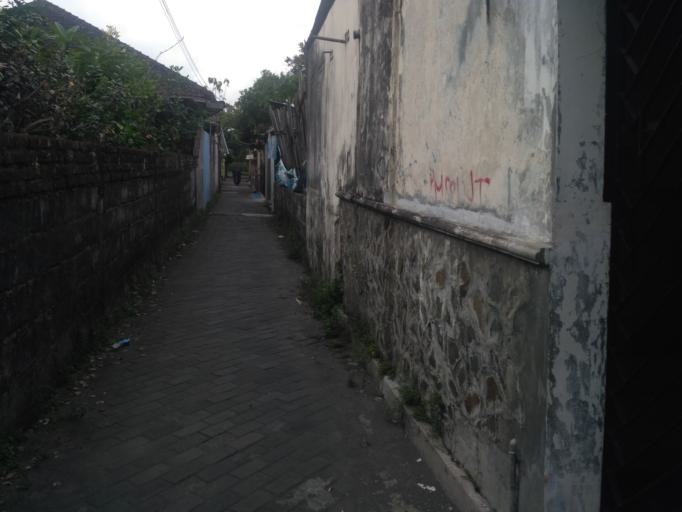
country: ID
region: Daerah Istimewa Yogyakarta
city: Melati
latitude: -7.7508
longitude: 110.3638
